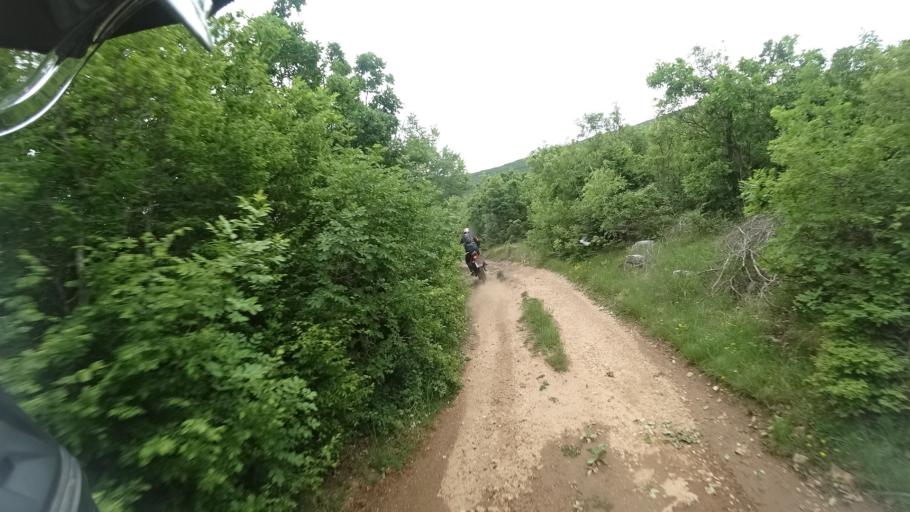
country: HR
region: Splitsko-Dalmatinska
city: Hrvace
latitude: 43.8939
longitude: 16.5290
